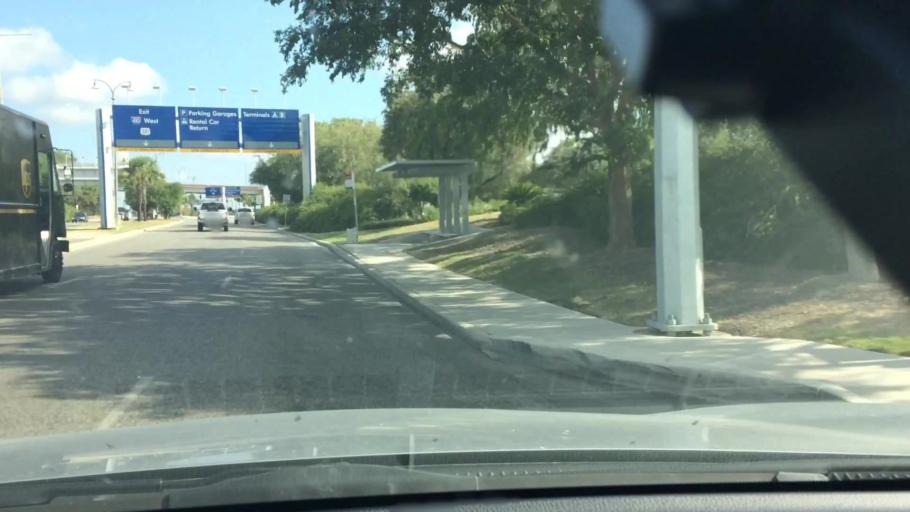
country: US
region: Texas
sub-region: Bexar County
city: Alamo Heights
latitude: 29.5218
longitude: -98.4767
